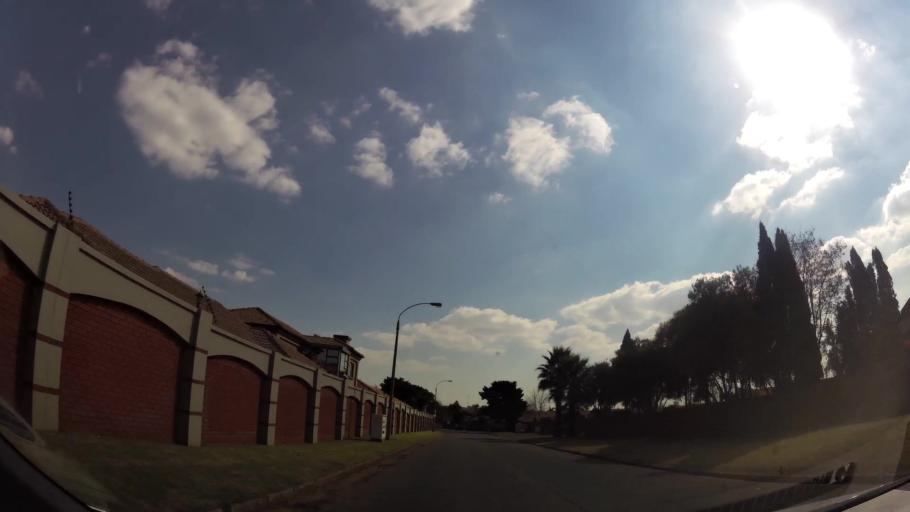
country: ZA
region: Gauteng
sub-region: Ekurhuleni Metropolitan Municipality
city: Boksburg
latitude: -26.1832
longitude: 28.2119
